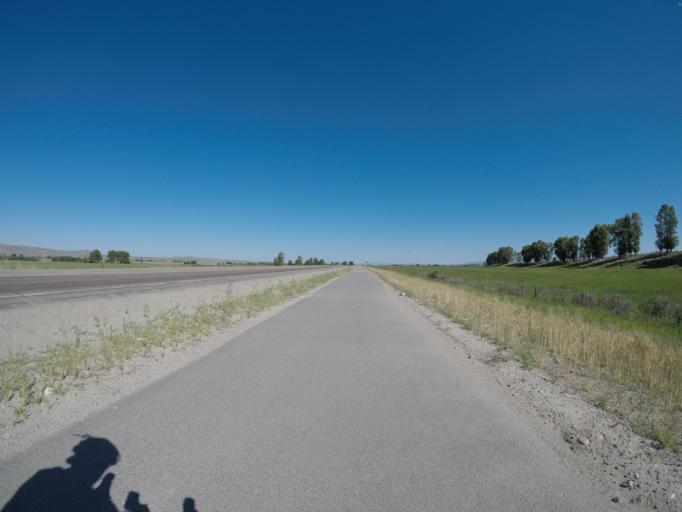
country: US
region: Wyoming
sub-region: Sublette County
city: Pinedale
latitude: 42.8161
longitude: -109.8365
